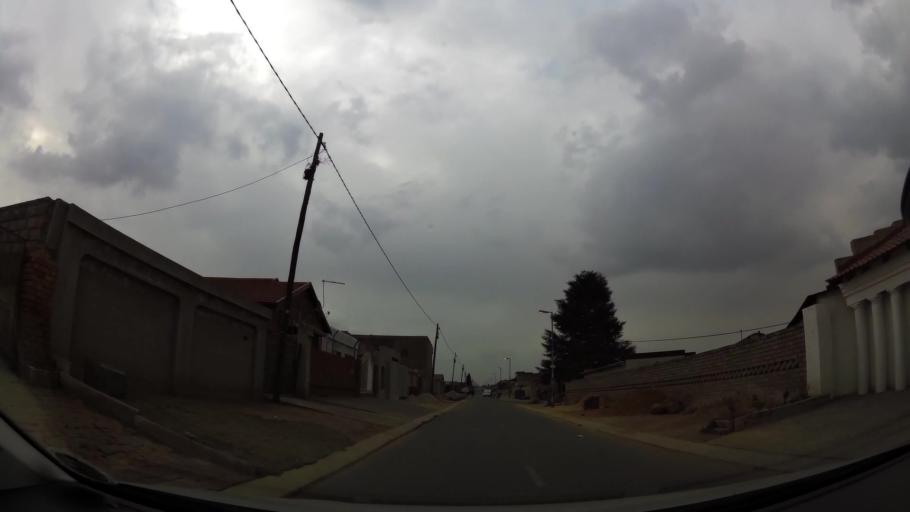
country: ZA
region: Gauteng
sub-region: City of Johannesburg Metropolitan Municipality
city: Soweto
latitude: -26.2645
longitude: 27.8640
